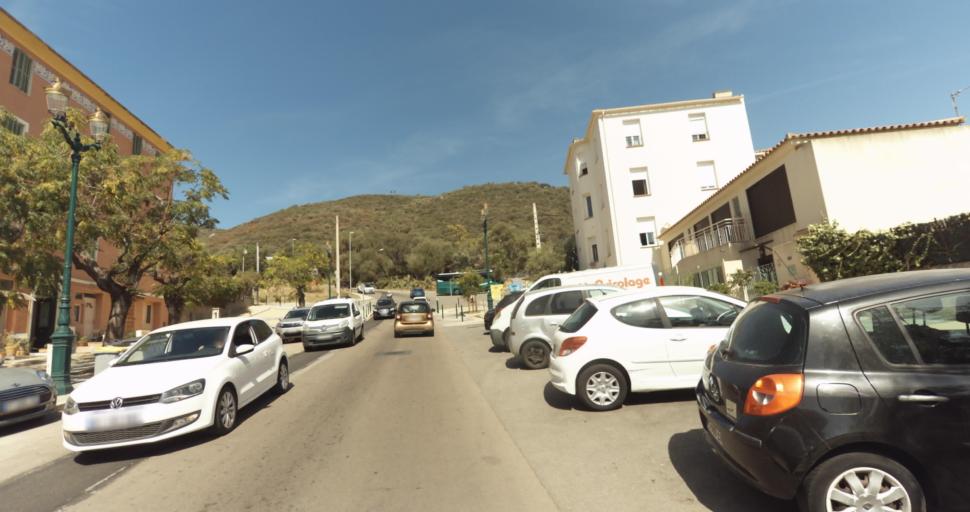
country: FR
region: Corsica
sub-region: Departement de la Corse-du-Sud
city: Ajaccio
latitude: 41.9152
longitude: 8.7243
